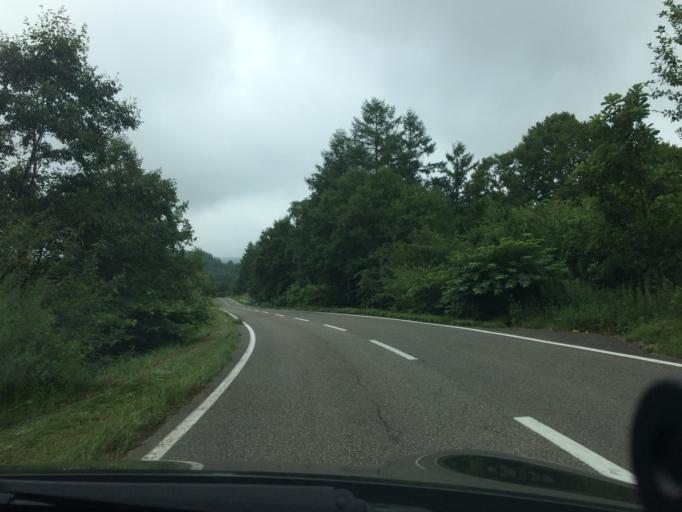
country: JP
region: Hokkaido
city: Otofuke
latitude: 42.9991
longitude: 143.0856
